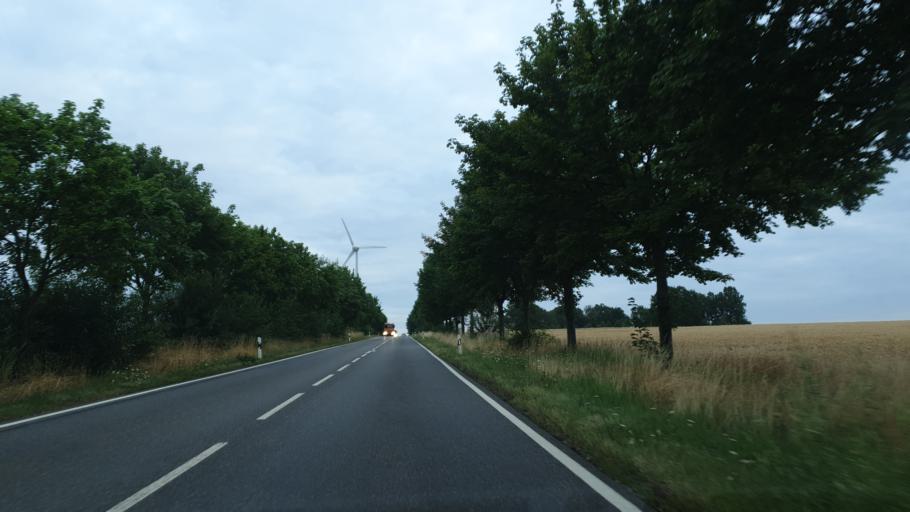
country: DE
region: Saxony
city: Sankt Egidien
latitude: 50.8107
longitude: 12.6333
